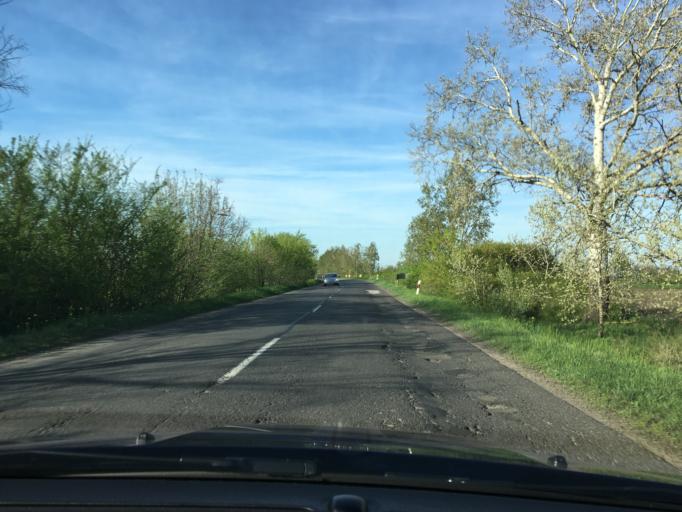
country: HU
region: Bekes
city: Korostarcsa
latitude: 46.8942
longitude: 21.0432
